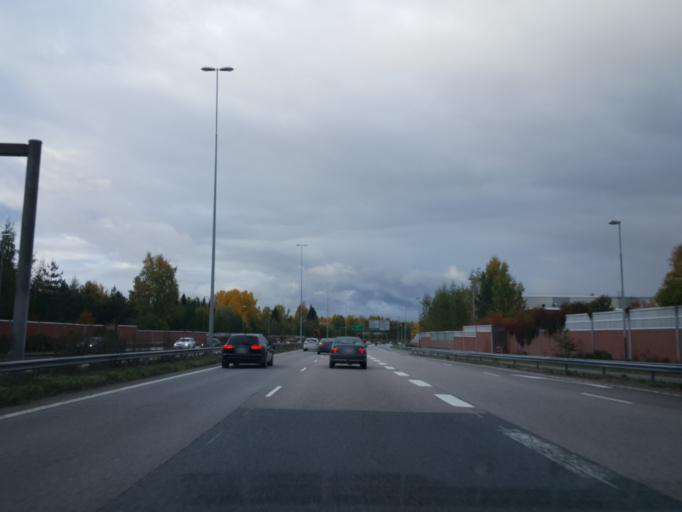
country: FI
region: Uusimaa
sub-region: Helsinki
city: Helsinki
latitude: 60.2479
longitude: 24.9484
